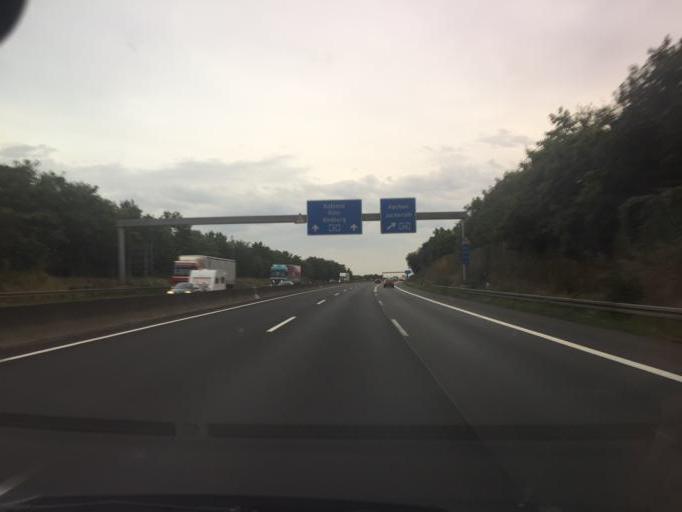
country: DE
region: North Rhine-Westphalia
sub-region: Regierungsbezirk Koln
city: Titz
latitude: 51.0525
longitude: 6.4488
